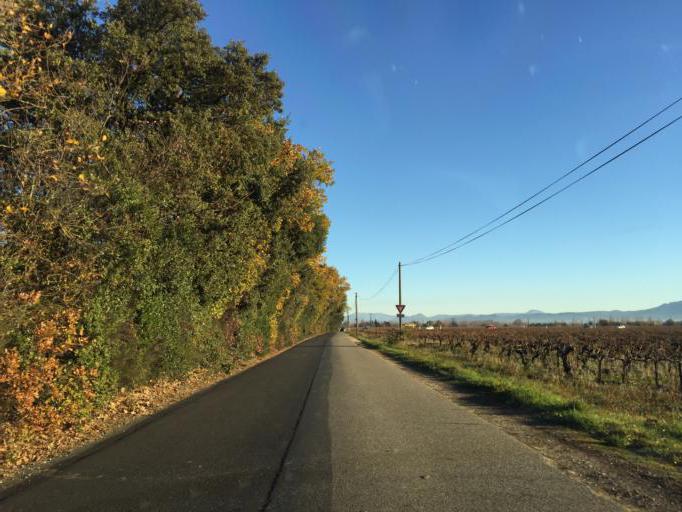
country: FR
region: Provence-Alpes-Cote d'Azur
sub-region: Departement du Vaucluse
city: Jonquieres
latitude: 44.1167
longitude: 4.8693
